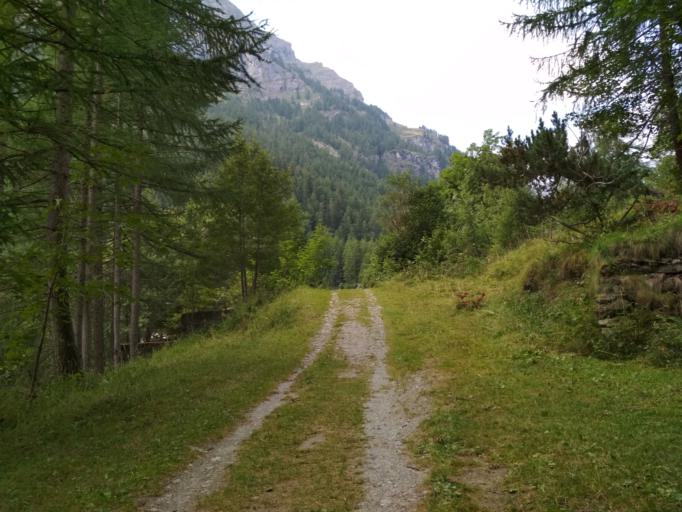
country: IT
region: Aosta Valley
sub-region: Valle d'Aosta
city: Gressoney-La-Trinite
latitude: 45.8148
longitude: 7.8278
